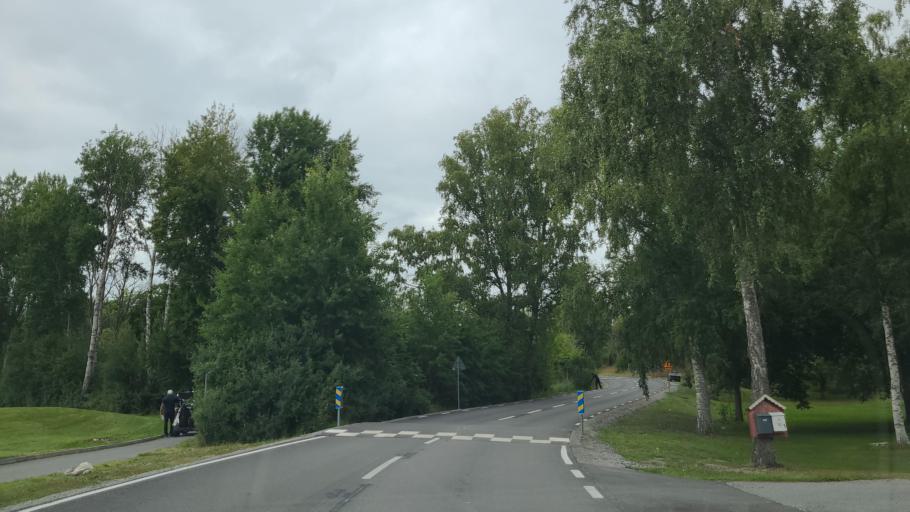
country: SE
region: Stockholm
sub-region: Upplands-Bro Kommun
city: Bro
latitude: 59.5016
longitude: 17.6258
